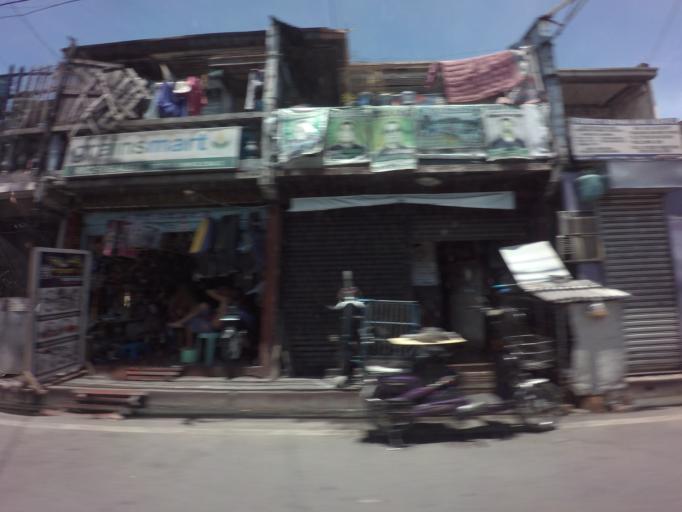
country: PH
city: Sambayanihan People's Village
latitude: 14.4826
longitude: 120.9831
